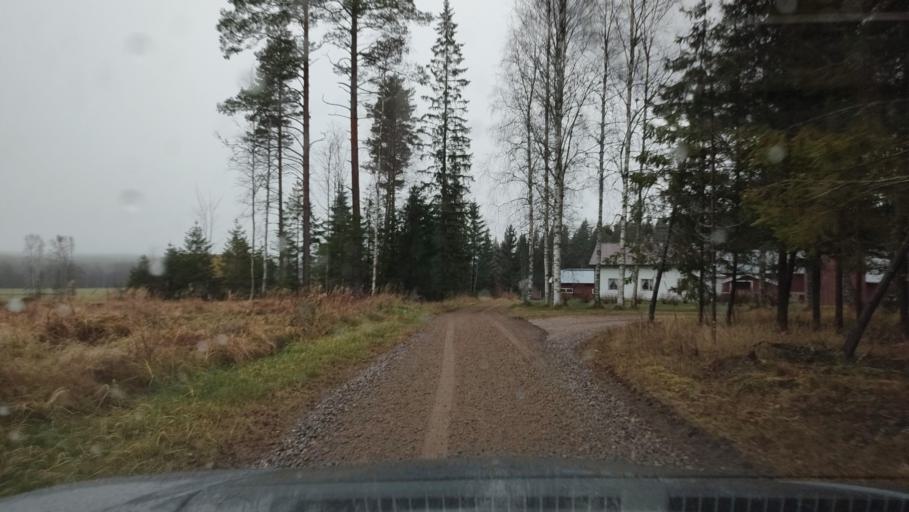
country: FI
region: Southern Ostrobothnia
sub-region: Suupohja
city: Karijoki
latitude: 62.1993
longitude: 21.7715
